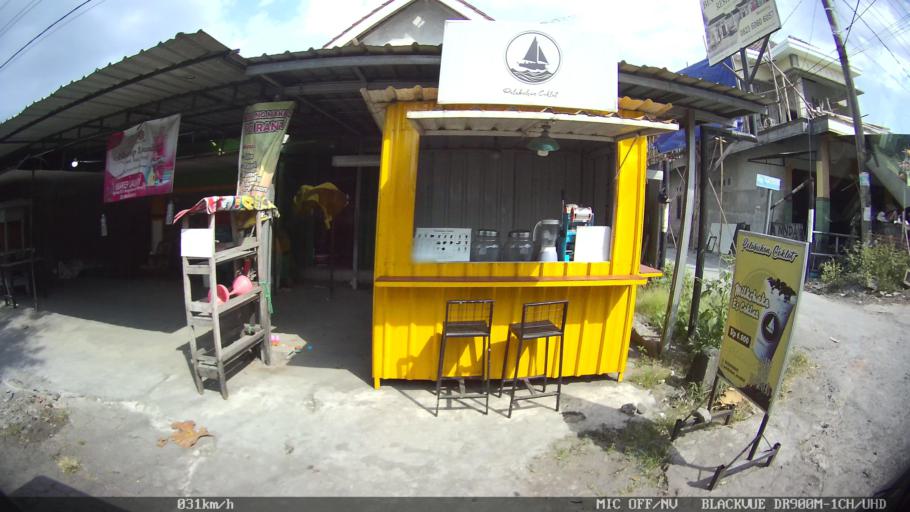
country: ID
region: Daerah Istimewa Yogyakarta
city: Kasihan
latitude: -7.8318
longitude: 110.3150
